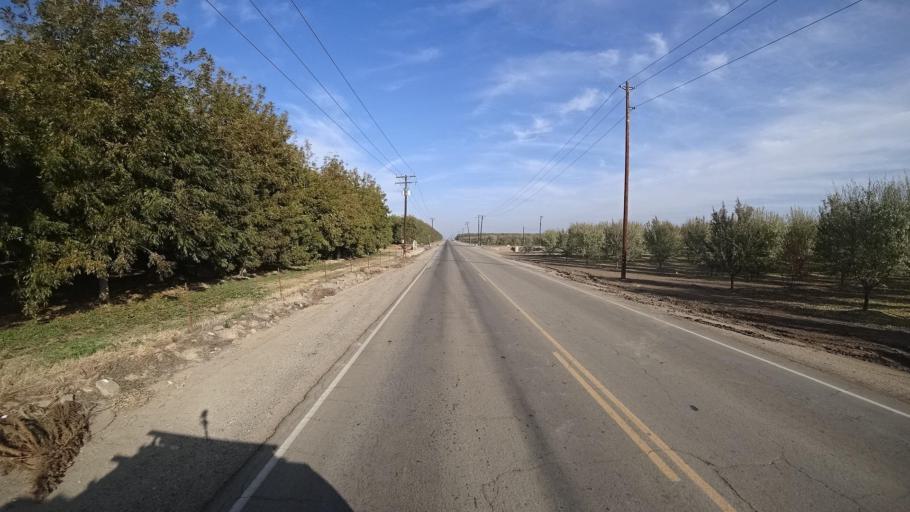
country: US
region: California
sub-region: Kern County
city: McFarland
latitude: 35.6300
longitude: -119.2044
